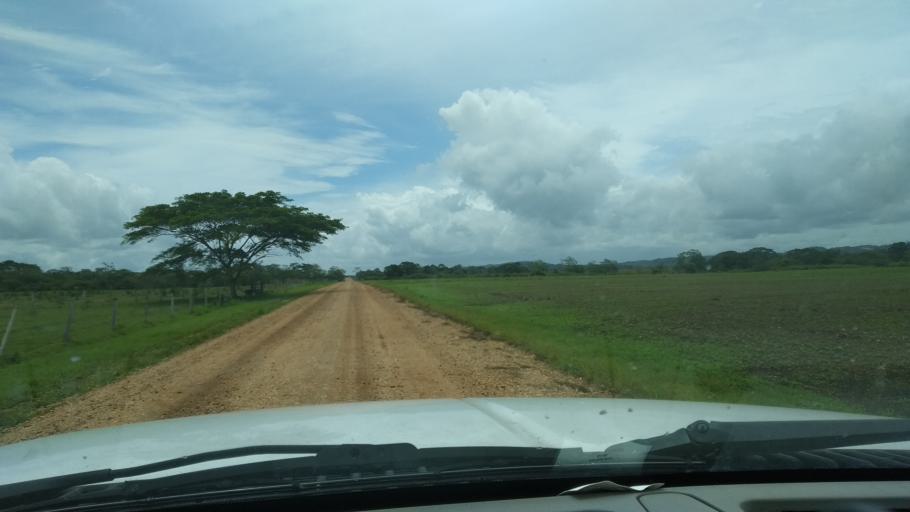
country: BZ
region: Cayo
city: San Ignacio
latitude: 17.2263
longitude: -88.9806
